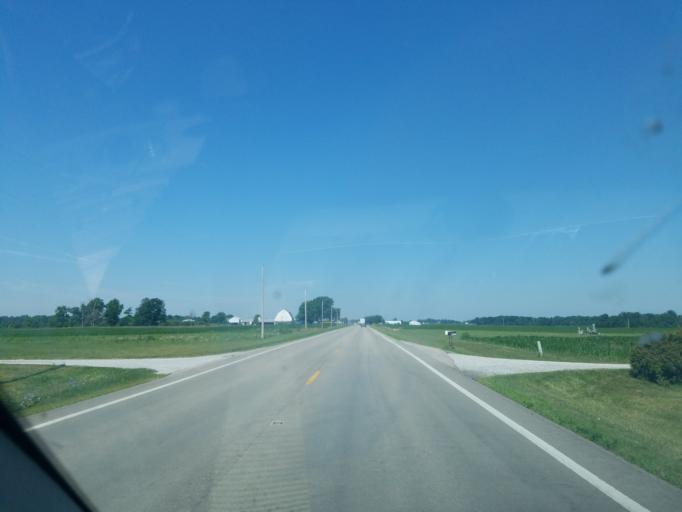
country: US
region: Ohio
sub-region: Shelby County
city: Botkins
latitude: 40.4387
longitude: -84.2296
